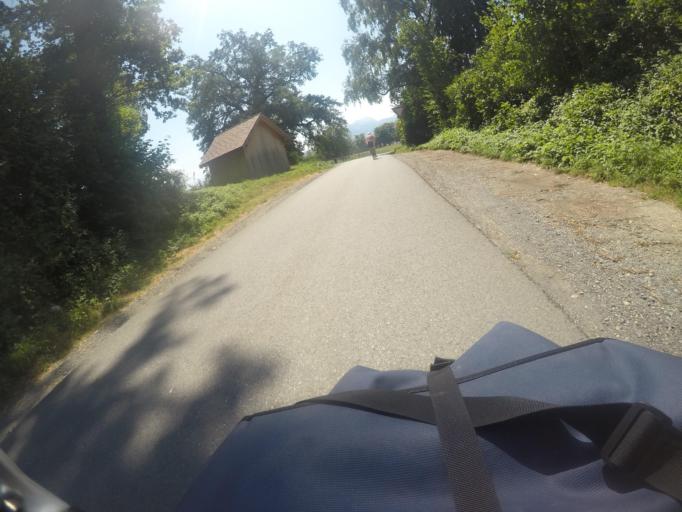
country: CH
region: Saint Gallen
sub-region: Wahlkreis Rheintal
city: Altstatten
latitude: 47.3829
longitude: 9.5677
